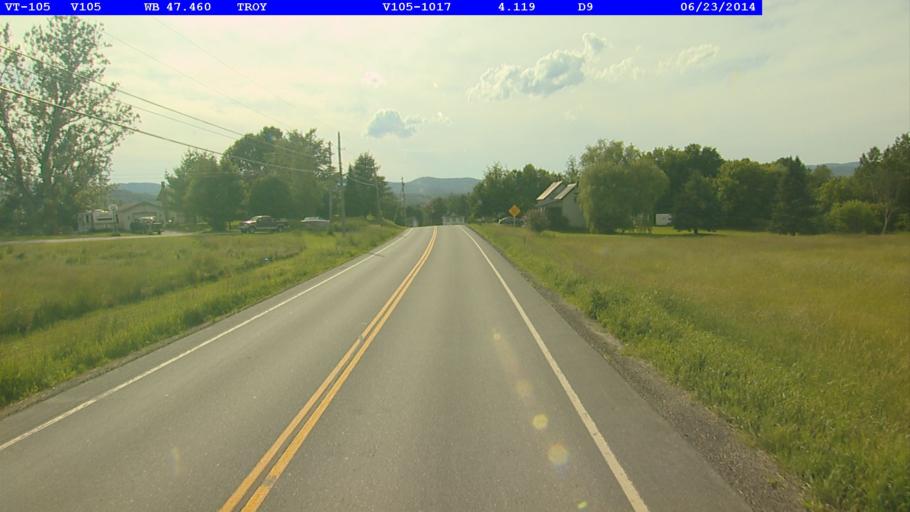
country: US
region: Vermont
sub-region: Orleans County
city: Newport
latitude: 44.9912
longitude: -72.3755
